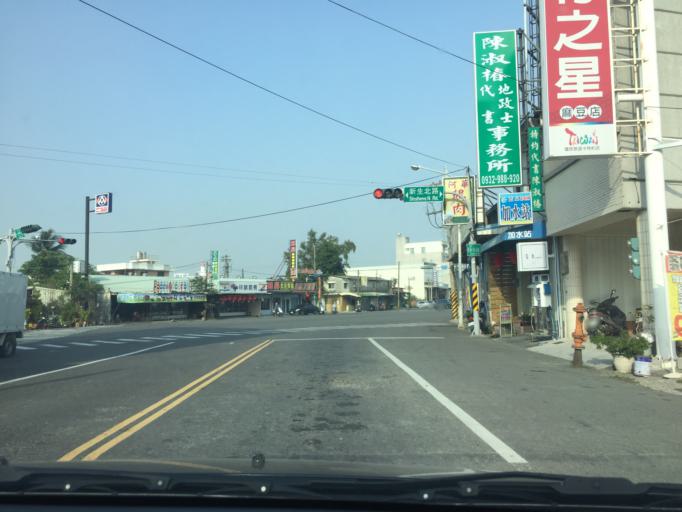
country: TW
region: Taiwan
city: Xinying
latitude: 23.1894
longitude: 120.2530
